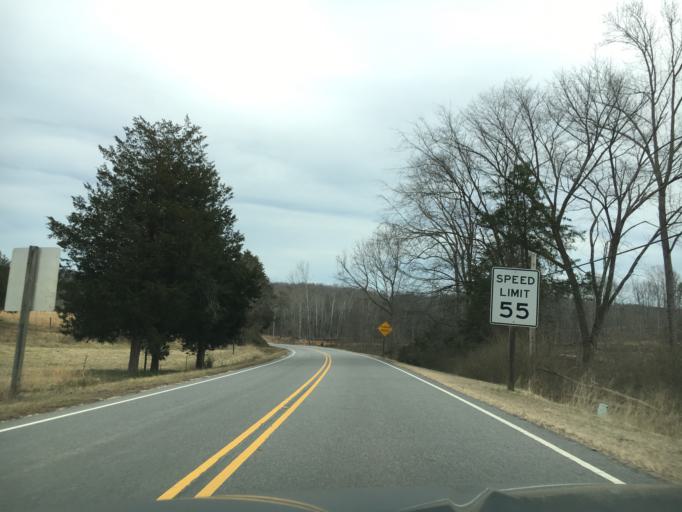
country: US
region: Virginia
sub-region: Charlotte County
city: Charlotte Court House
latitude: 37.0779
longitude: -78.7407
